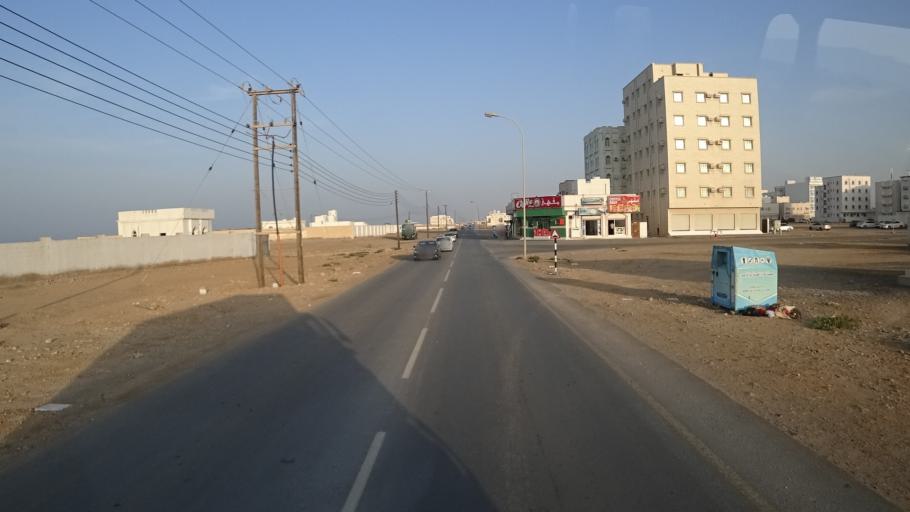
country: OM
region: Ash Sharqiyah
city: Sur
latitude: 22.6090
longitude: 59.4717
